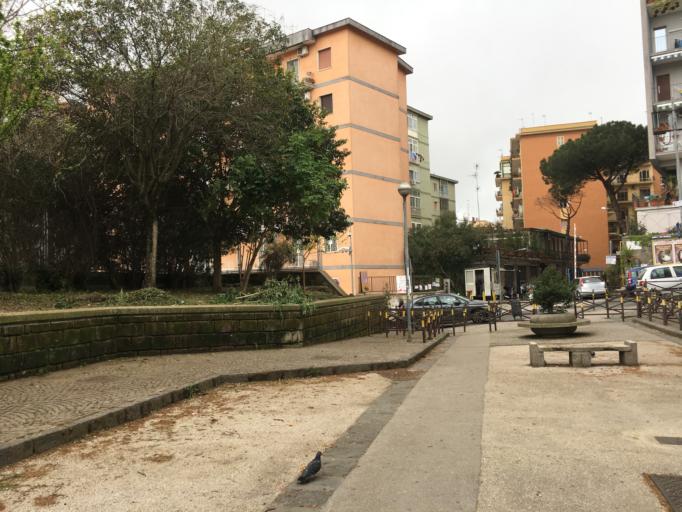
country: IT
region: Campania
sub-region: Provincia di Napoli
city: Napoli
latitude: 40.8557
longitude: 14.2236
